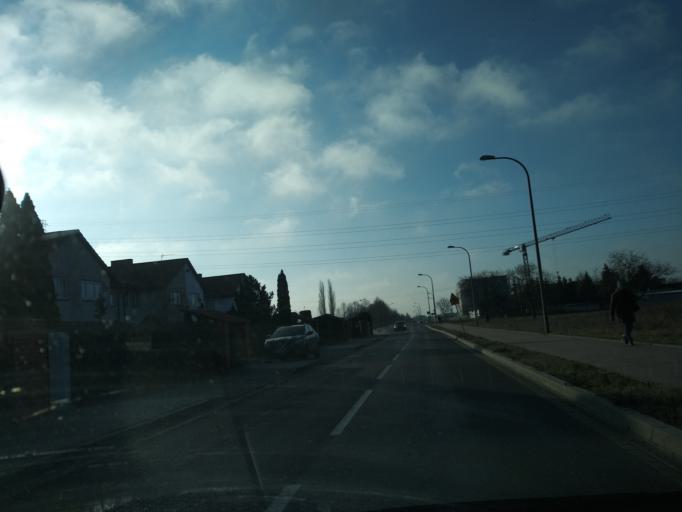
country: PL
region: Masovian Voivodeship
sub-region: Powiat piaseczynski
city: Mysiadlo
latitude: 52.0897
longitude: 21.0129
